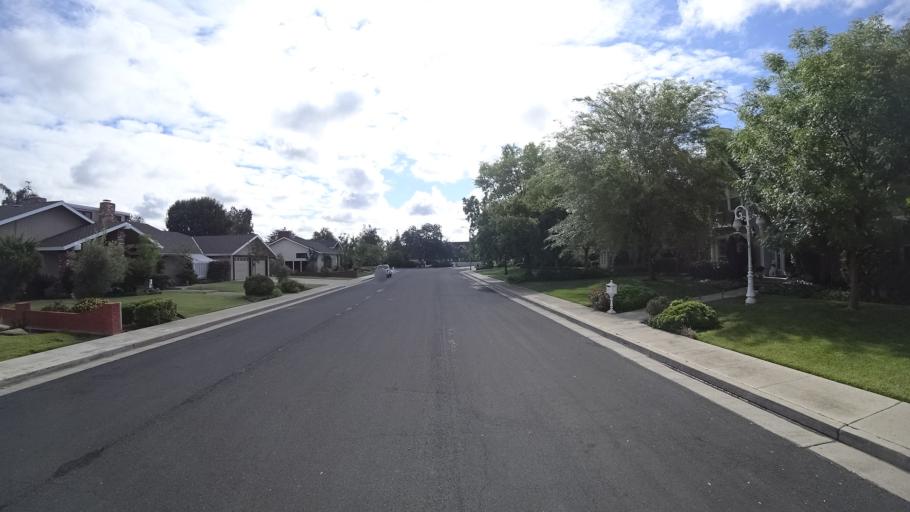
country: US
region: California
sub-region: Kings County
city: Lucerne
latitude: 36.3589
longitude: -119.6482
